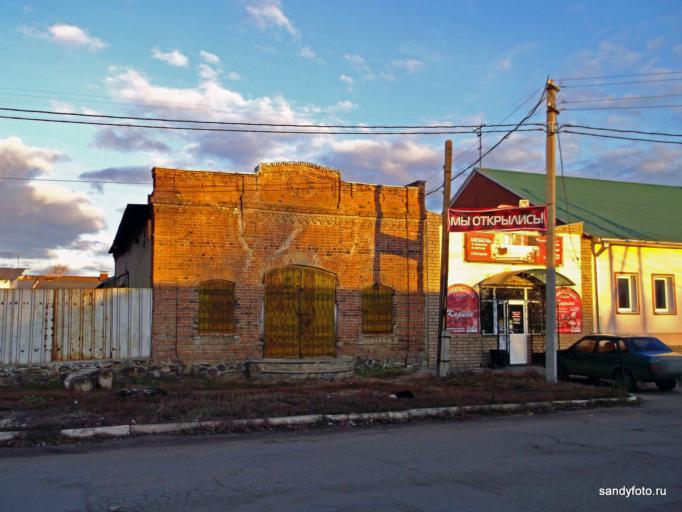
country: RU
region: Chelyabinsk
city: Troitsk
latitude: 54.0858
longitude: 61.5529
